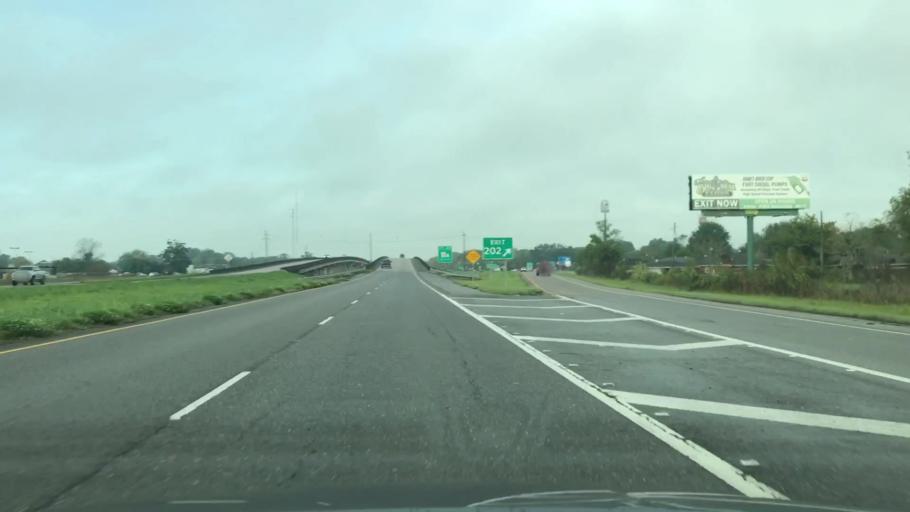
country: US
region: Louisiana
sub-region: Terrebonne Parish
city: Gray
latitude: 29.6803
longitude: -90.7784
